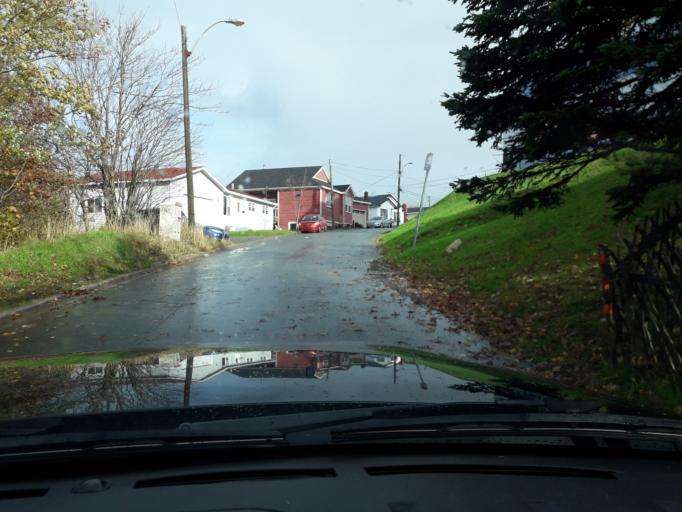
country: CA
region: Newfoundland and Labrador
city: St. John's
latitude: 47.5714
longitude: -52.6950
